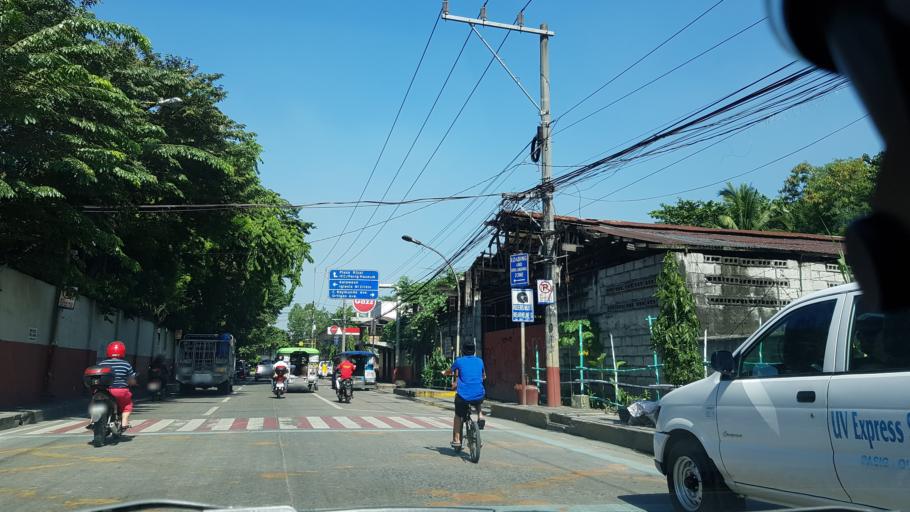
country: PH
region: Calabarzon
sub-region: Province of Rizal
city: Pateros
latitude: 14.5603
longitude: 121.0820
